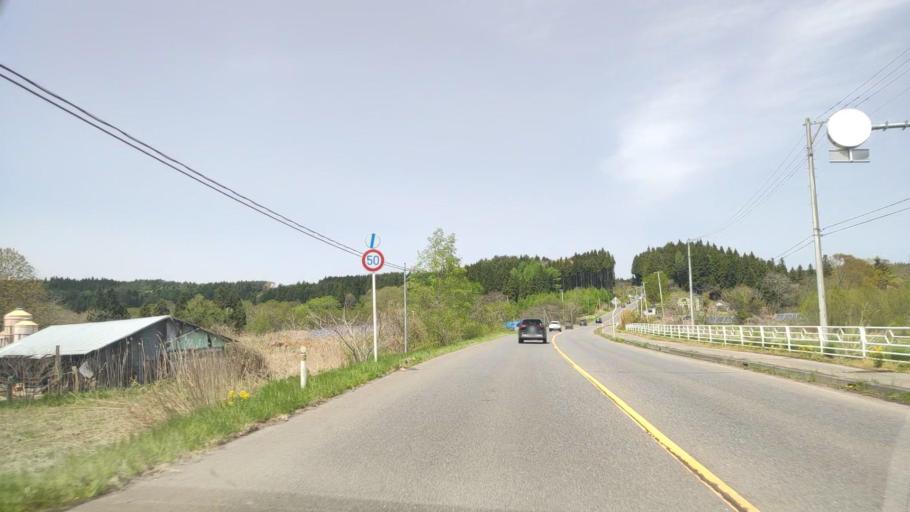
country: JP
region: Aomori
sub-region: Misawa Shi
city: Inuotose
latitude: 40.5621
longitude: 141.3828
